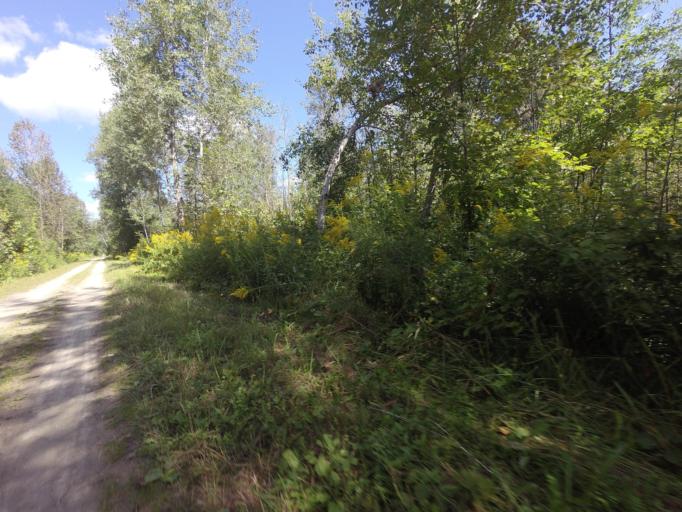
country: CA
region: Ontario
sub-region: Wellington County
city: Guelph
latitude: 43.7500
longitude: -80.3189
